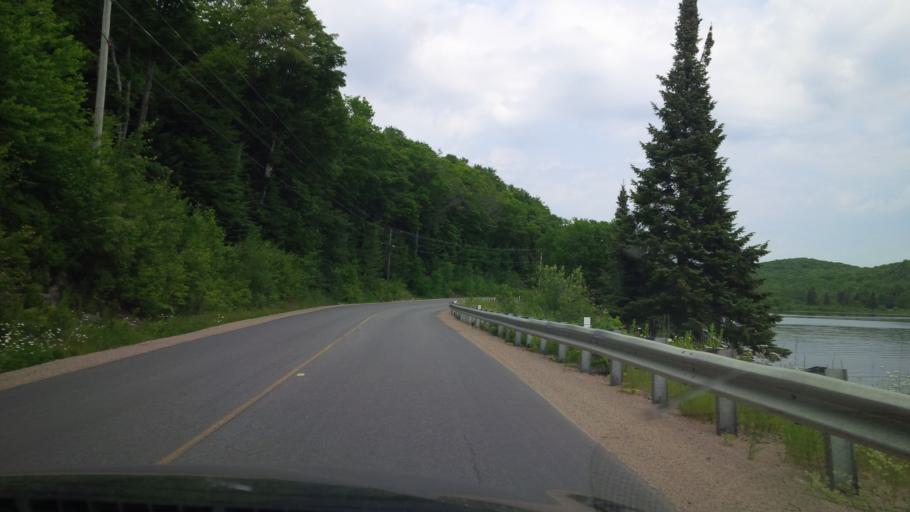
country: CA
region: Ontario
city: Huntsville
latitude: 45.5817
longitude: -79.2163
